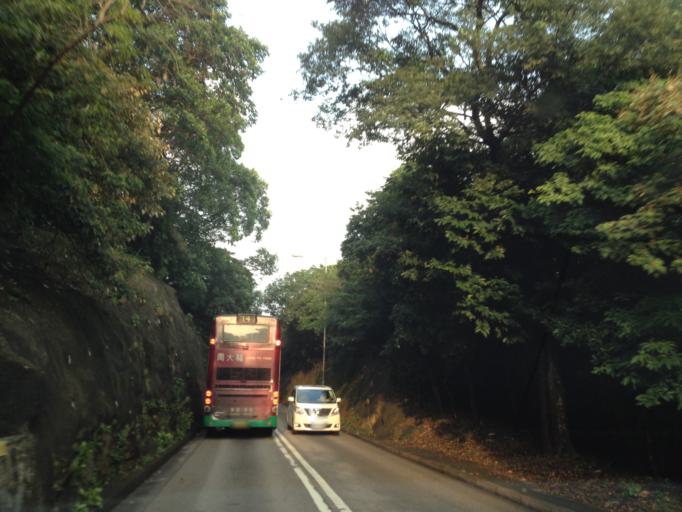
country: HK
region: Wanchai
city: Wan Chai
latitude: 22.2623
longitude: 114.2288
